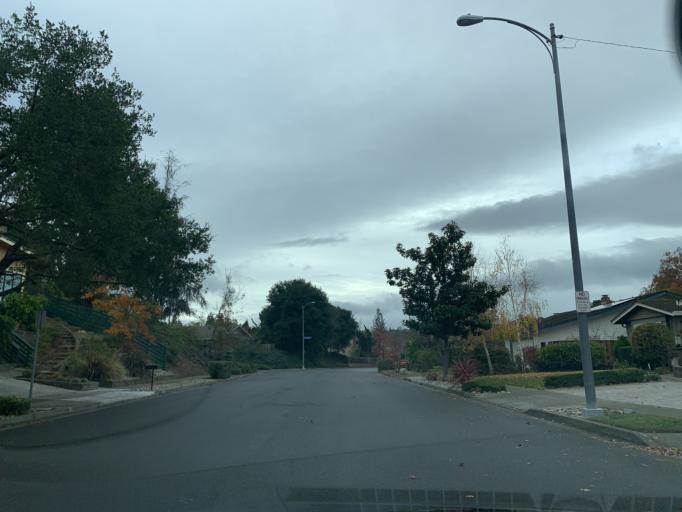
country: US
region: California
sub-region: Santa Clara County
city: Cupertino
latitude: 37.3273
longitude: -122.0593
